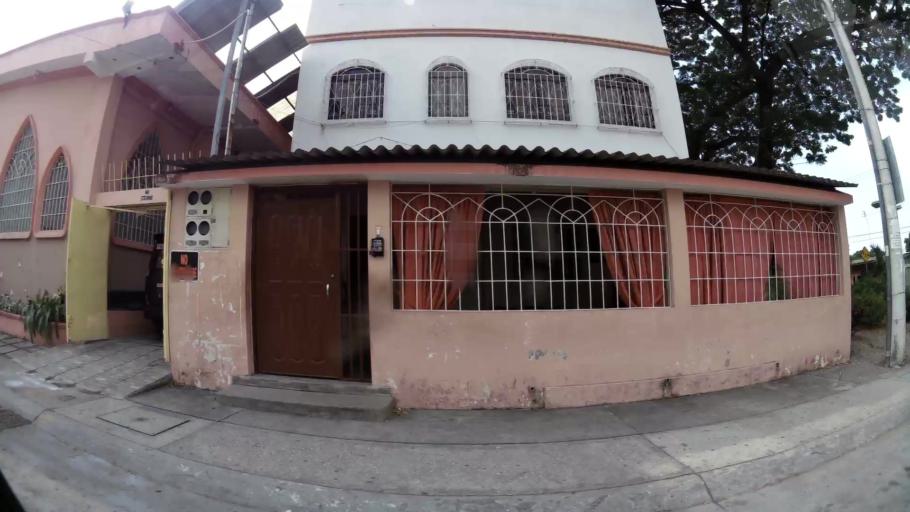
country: EC
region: Guayas
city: Eloy Alfaro
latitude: -2.1165
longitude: -79.8915
